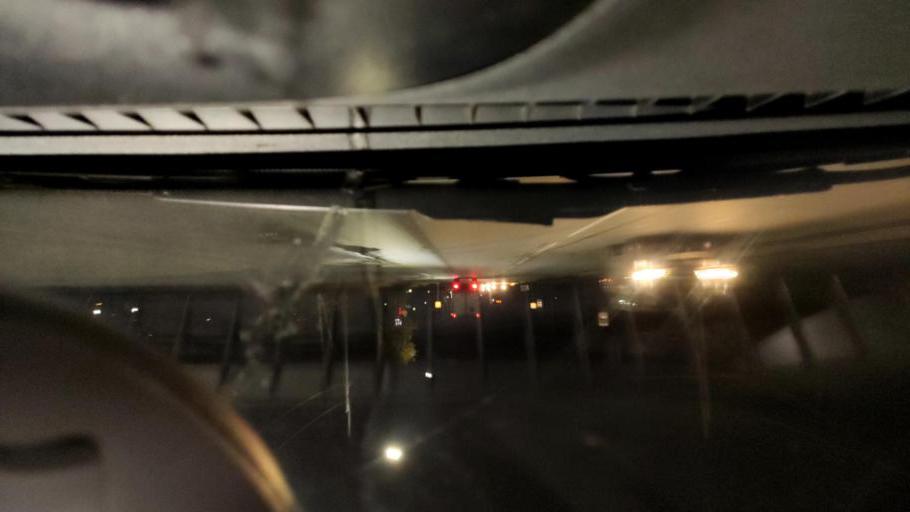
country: RU
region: Perm
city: Kondratovo
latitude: 57.9331
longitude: 56.1244
